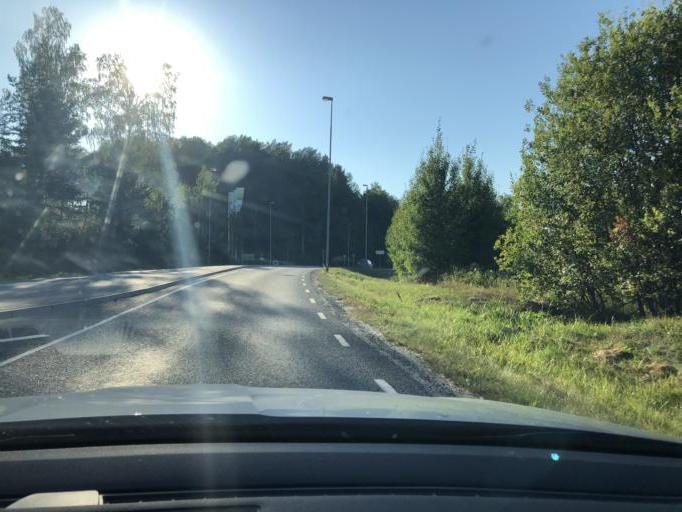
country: SE
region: Stockholm
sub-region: Sodertalje Kommun
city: Soedertaelje
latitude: 59.1849
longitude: 17.5852
